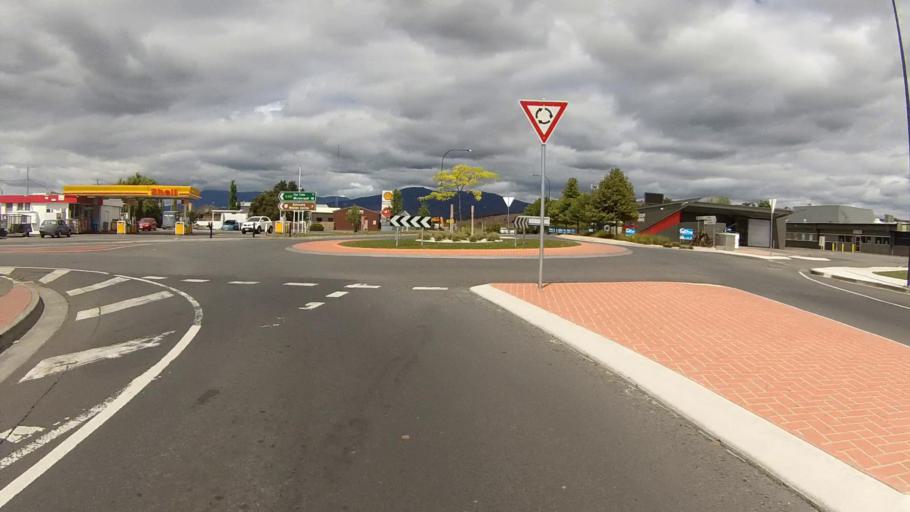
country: AU
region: Tasmania
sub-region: Brighton
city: Bridgewater
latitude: -42.6998
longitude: 147.2514
